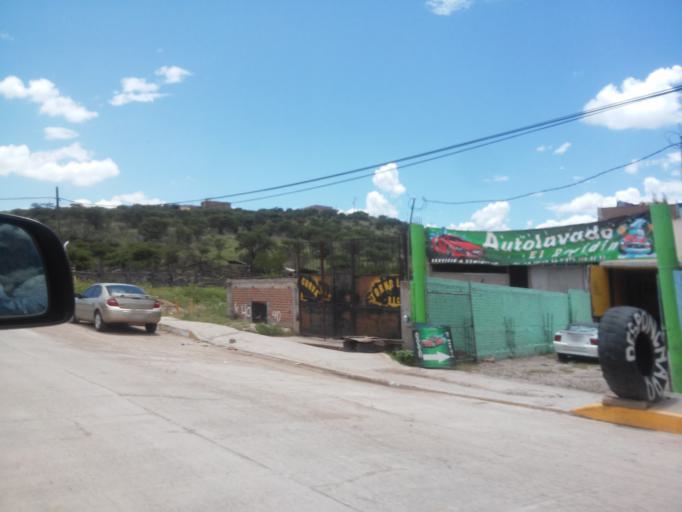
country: MX
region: Durango
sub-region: Santiago Papasquiaro
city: Santiago Papasquiaro
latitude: 25.0621
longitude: -105.4266
